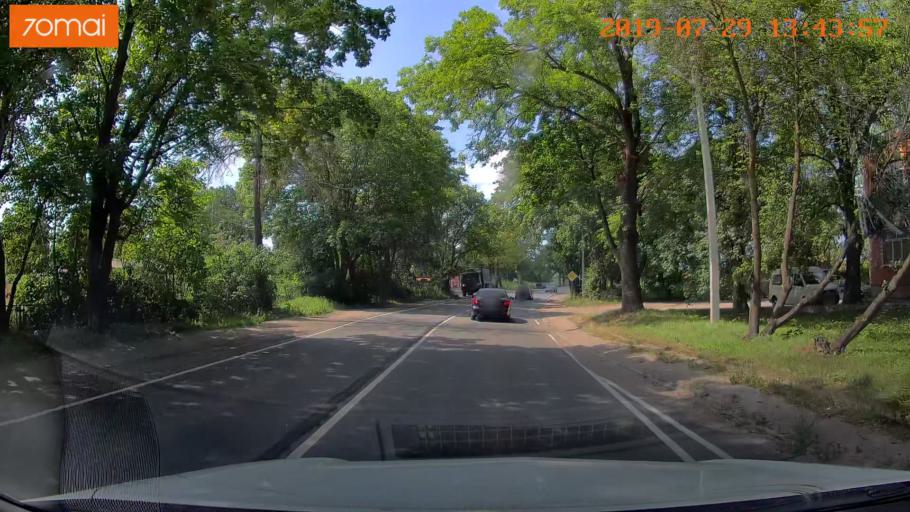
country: RU
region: Kaliningrad
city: Svetlyy
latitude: 54.7371
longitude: 20.0945
